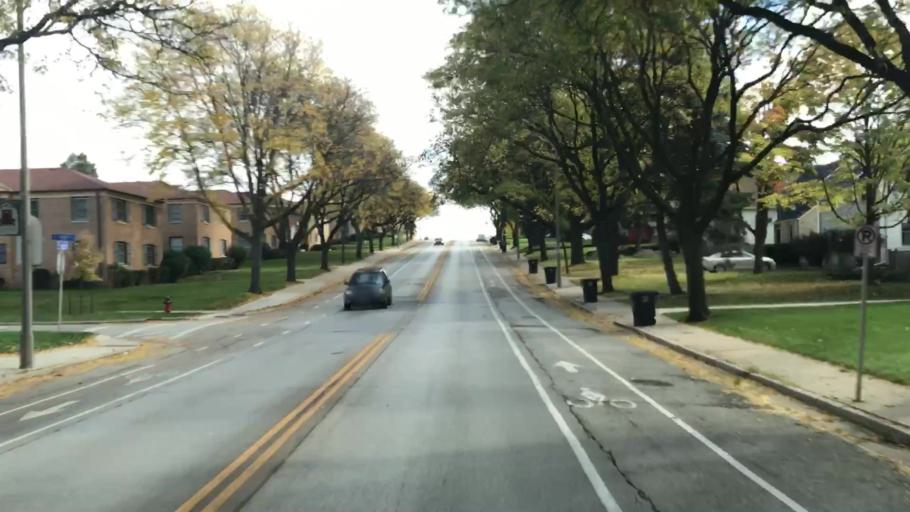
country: US
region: Wisconsin
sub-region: Milwaukee County
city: Wauwatosa
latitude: 43.0607
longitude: -88.0130
